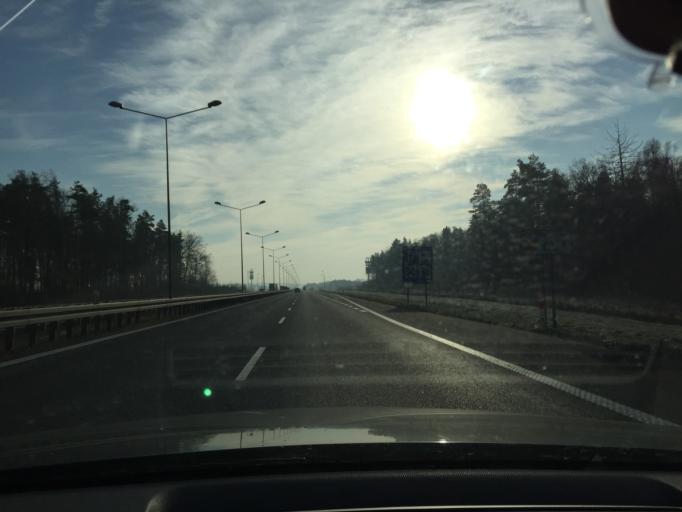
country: PL
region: Silesian Voivodeship
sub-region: Powiat gliwicki
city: Sosnicowice
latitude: 50.3174
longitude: 18.5493
